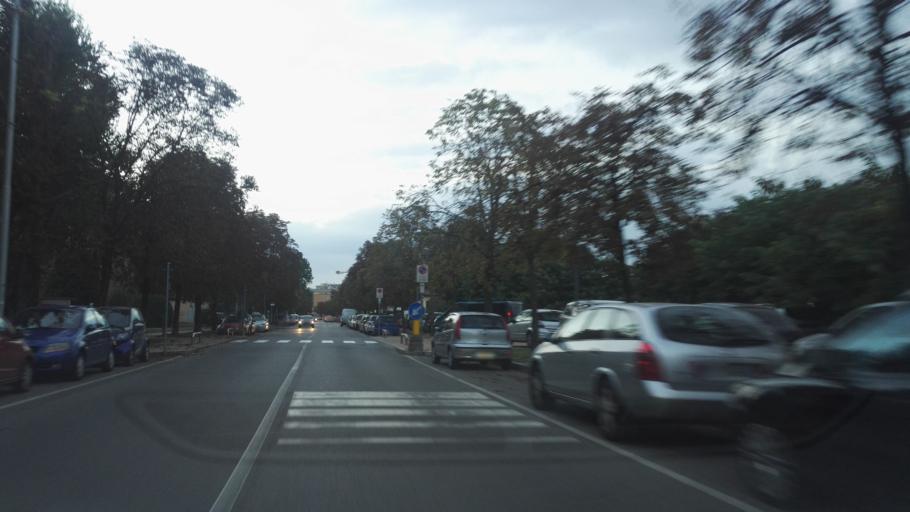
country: IT
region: Lombardy
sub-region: Citta metropolitana di Milano
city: San Giuliano Milanese
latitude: 45.3867
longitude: 9.3021
